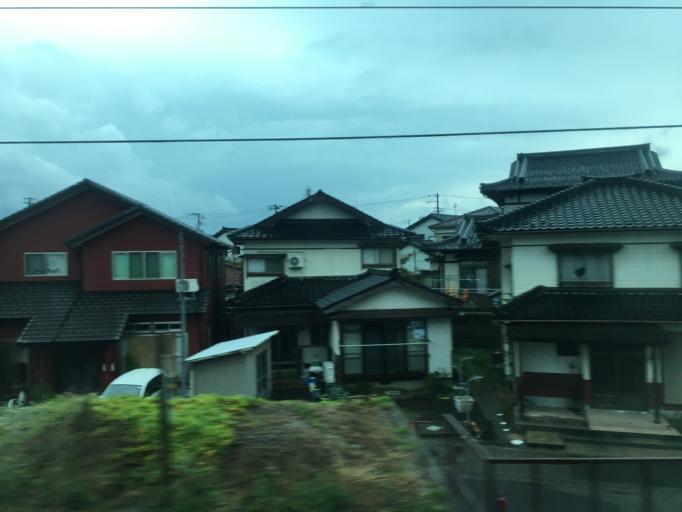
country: JP
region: Yamagata
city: Tsuruoka
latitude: 38.5579
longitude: 139.5494
